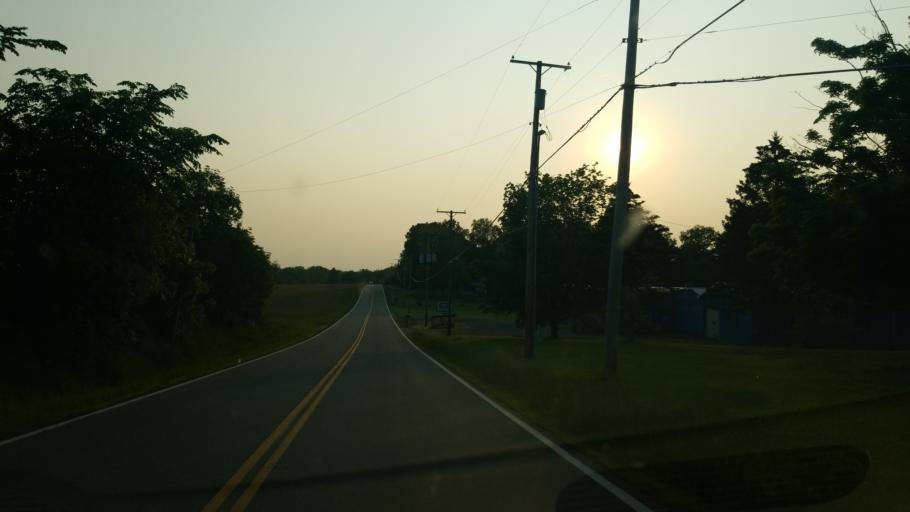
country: US
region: Ohio
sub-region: Ashland County
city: Ashland
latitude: 40.9327
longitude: -82.3077
